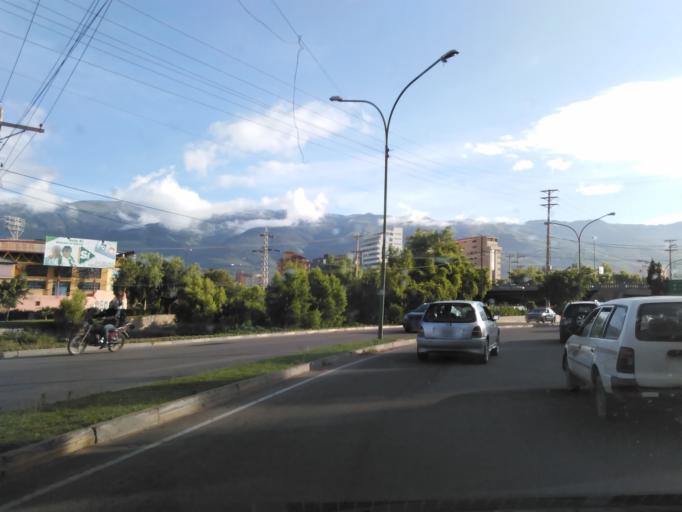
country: BO
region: Cochabamba
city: Cochabamba
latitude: -17.3823
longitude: -66.1610
